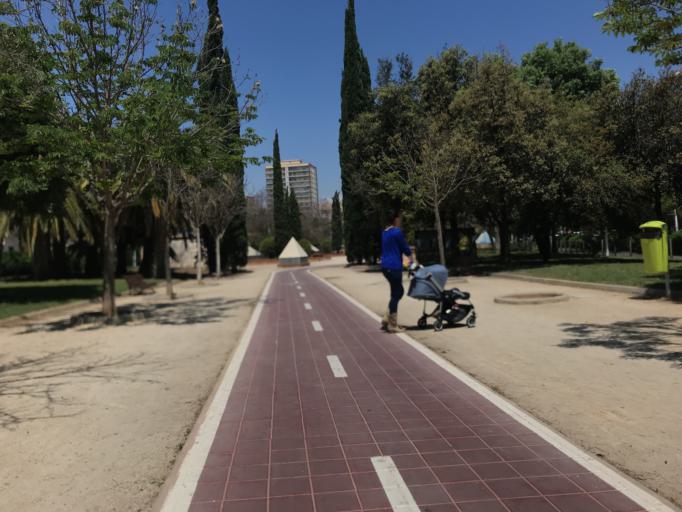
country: ES
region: Valencia
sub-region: Provincia de Valencia
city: Mislata
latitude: 39.4676
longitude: -0.4061
